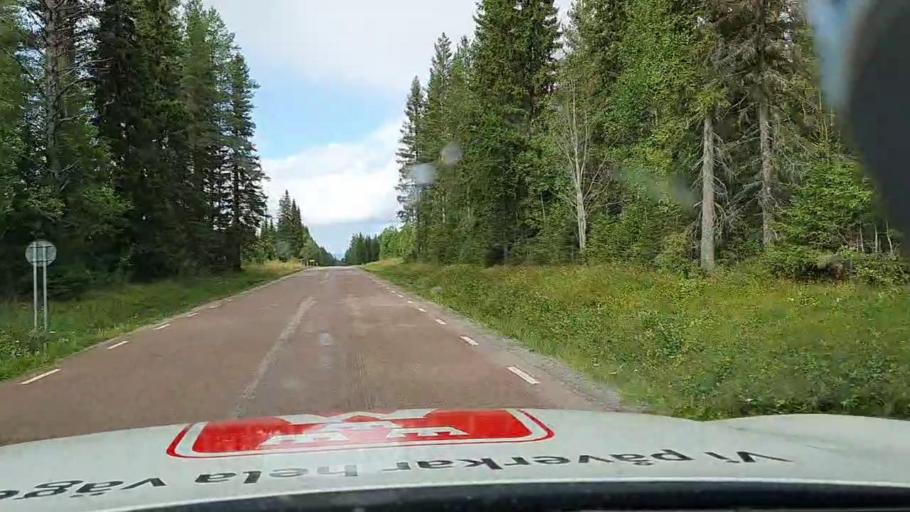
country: SE
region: Jaemtland
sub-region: Stroemsunds Kommun
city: Stroemsund
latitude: 63.8699
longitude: 15.3713
